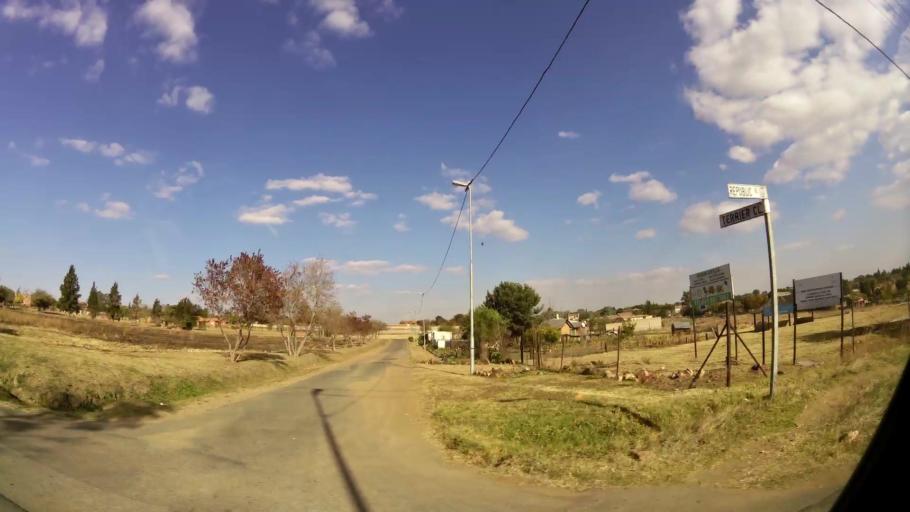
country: ZA
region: Gauteng
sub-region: City of Johannesburg Metropolitan Municipality
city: Midrand
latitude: -26.0179
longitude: 28.1524
